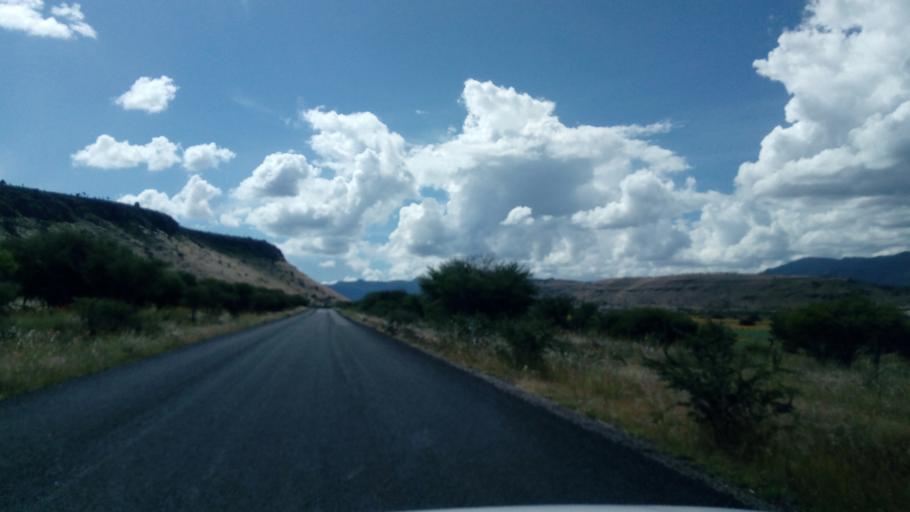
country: MX
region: Durango
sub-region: Durango
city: Jose Refugio Salcido
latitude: 23.8378
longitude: -104.4807
